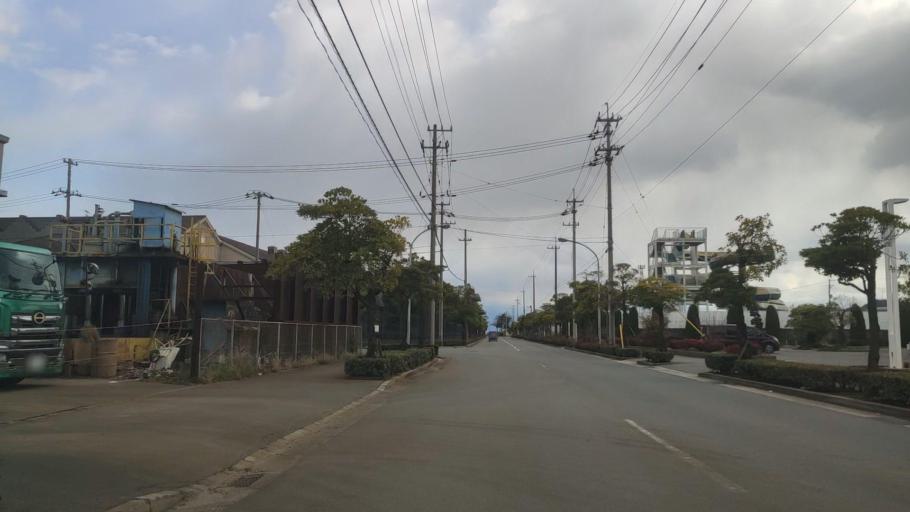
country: JP
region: Ehime
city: Saijo
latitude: 34.0482
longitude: 133.0269
